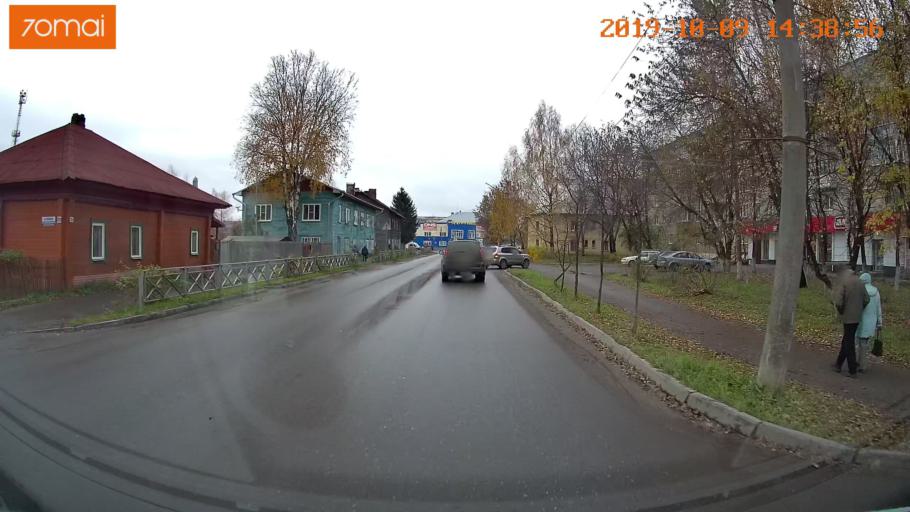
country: RU
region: Kostroma
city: Buy
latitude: 58.4779
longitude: 41.5378
